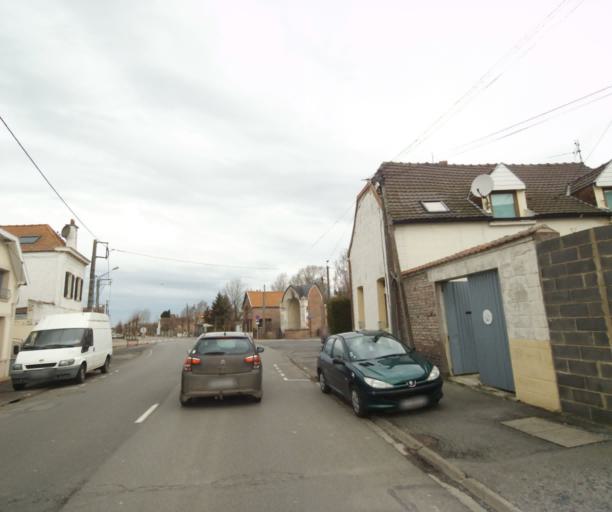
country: FR
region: Nord-Pas-de-Calais
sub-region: Departement du Nord
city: Curgies
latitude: 50.3315
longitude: 3.5990
